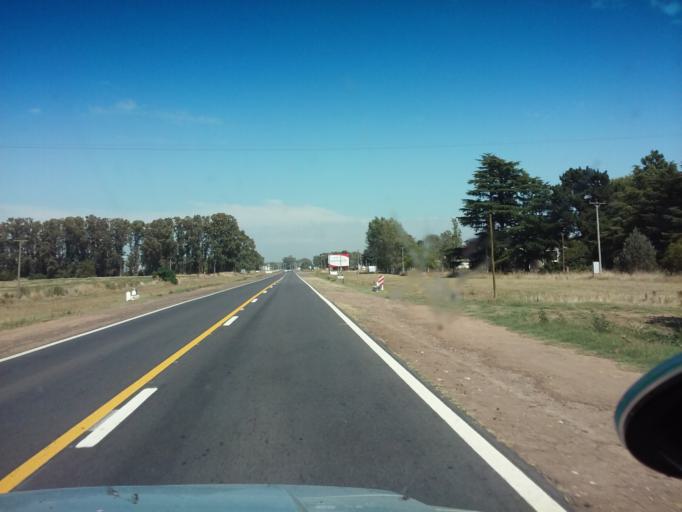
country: AR
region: Buenos Aires
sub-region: Partido de Nueve de Julio
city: Nueve de Julio
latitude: -35.4613
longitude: -60.8381
